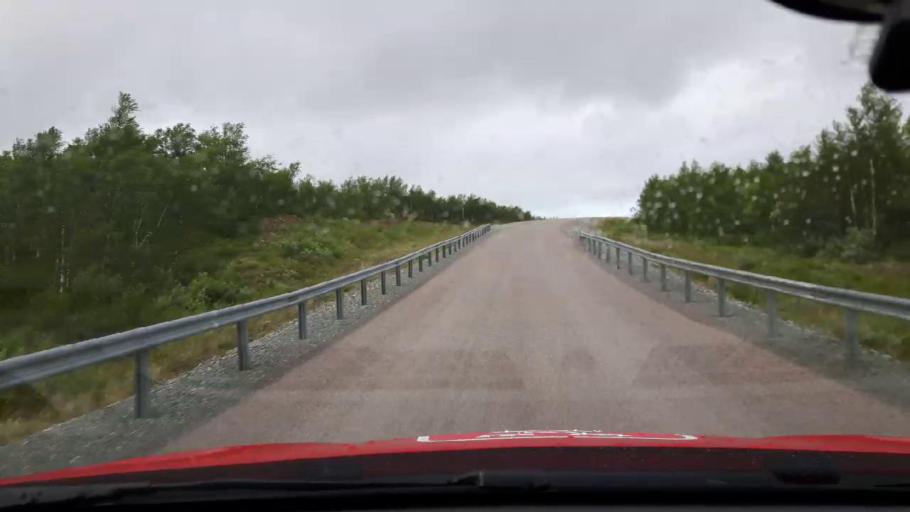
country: SE
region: Jaemtland
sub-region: Are Kommun
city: Are
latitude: 63.2186
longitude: 12.4106
